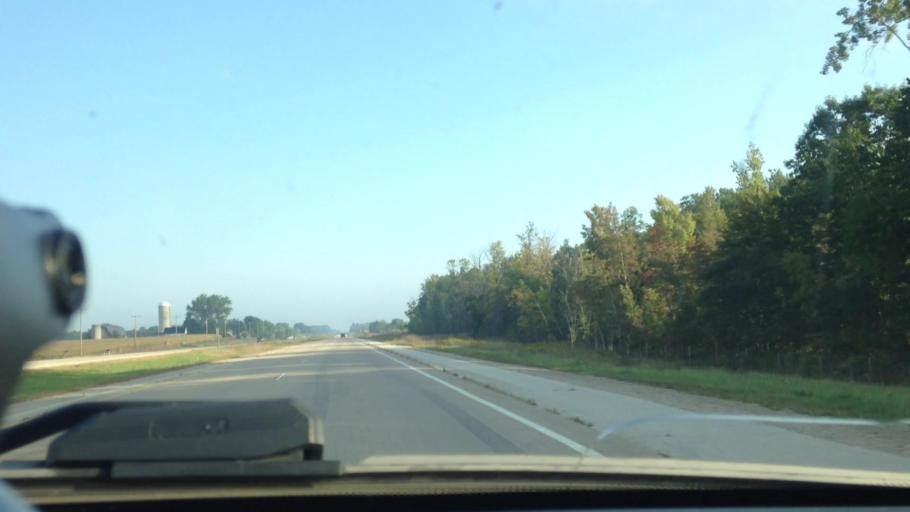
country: US
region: Wisconsin
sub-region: Oconto County
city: Oconto Falls
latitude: 45.0019
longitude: -88.0449
